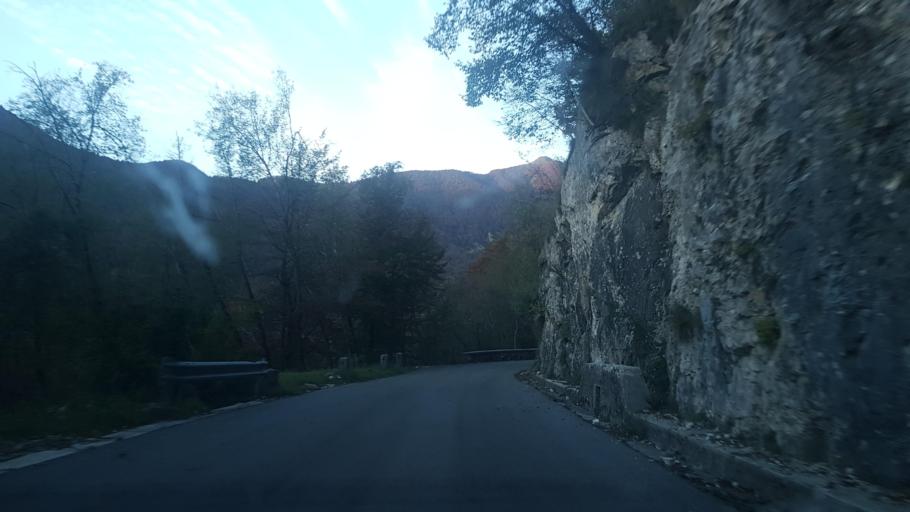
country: IT
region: Friuli Venezia Giulia
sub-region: Provincia di Udine
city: Preone
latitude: 46.3468
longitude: 12.8971
